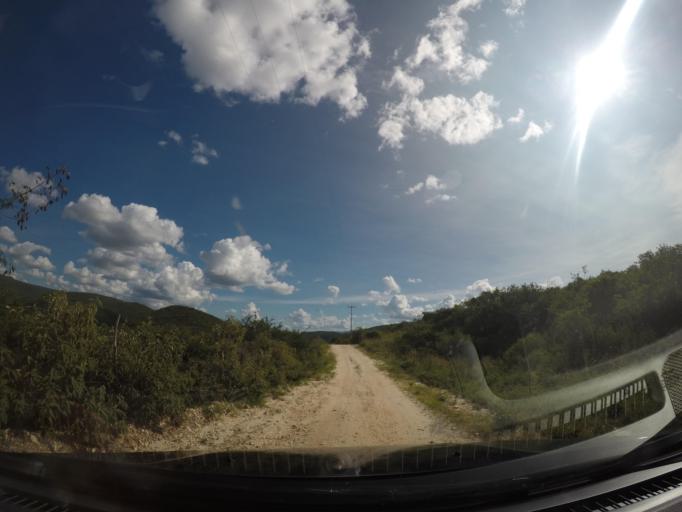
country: BR
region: Bahia
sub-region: Barra Da Estiva
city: Barra da Estiva
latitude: -13.2158
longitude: -41.5945
